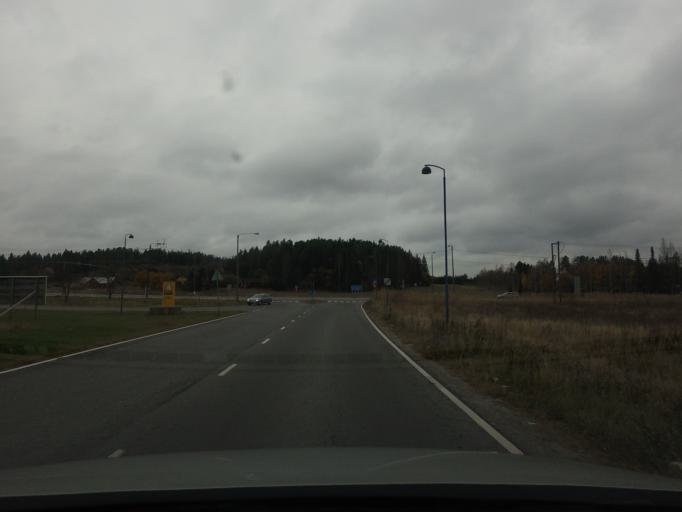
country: FI
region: Varsinais-Suomi
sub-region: Turku
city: Paimio
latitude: 60.4453
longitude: 22.6066
